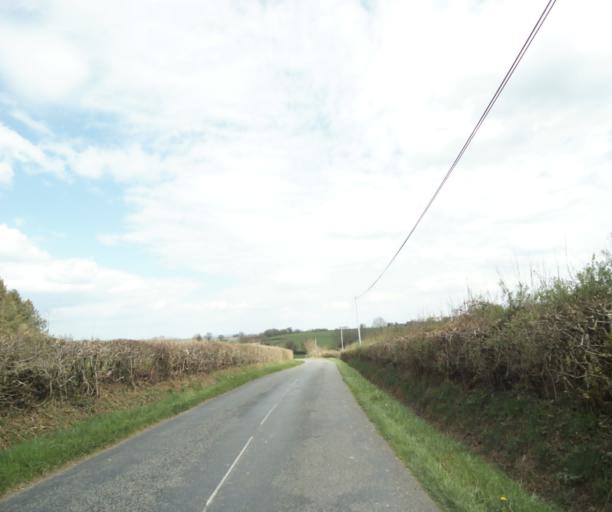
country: FR
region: Bourgogne
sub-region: Departement de Saone-et-Loire
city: Palinges
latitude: 46.5389
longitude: 4.2140
